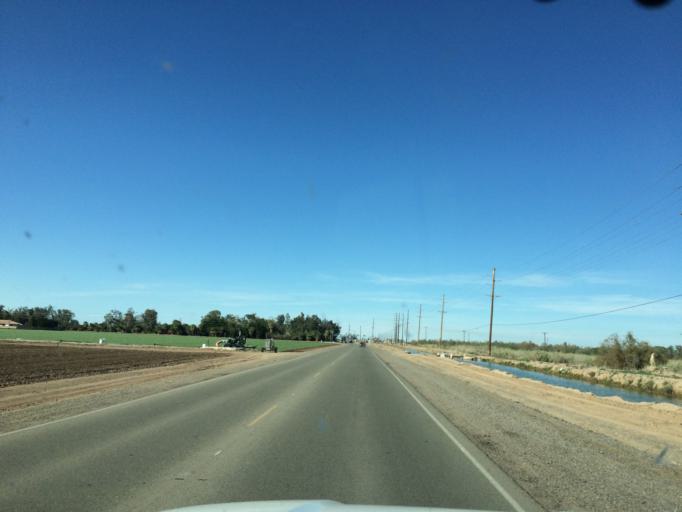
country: US
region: California
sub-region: Imperial County
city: Heber
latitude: 32.7480
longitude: -115.5347
